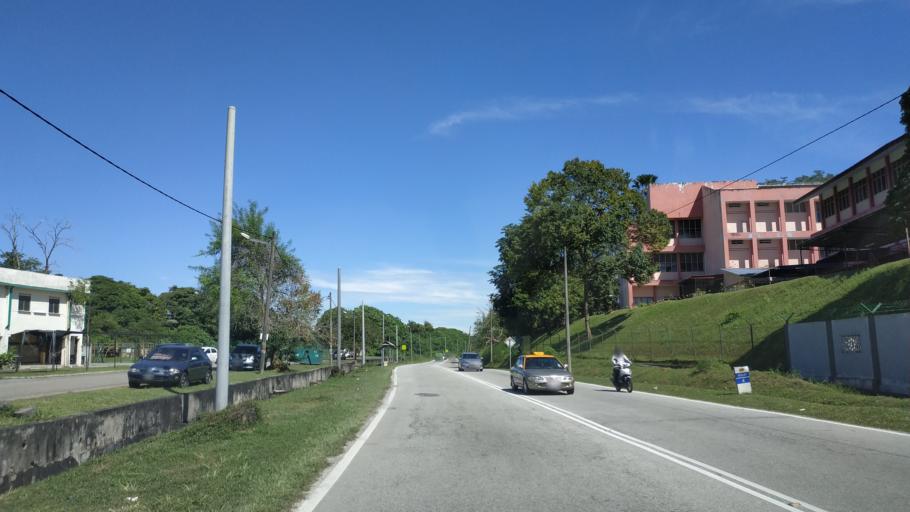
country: MY
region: Kedah
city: Kulim
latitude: 5.3384
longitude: 100.5378
